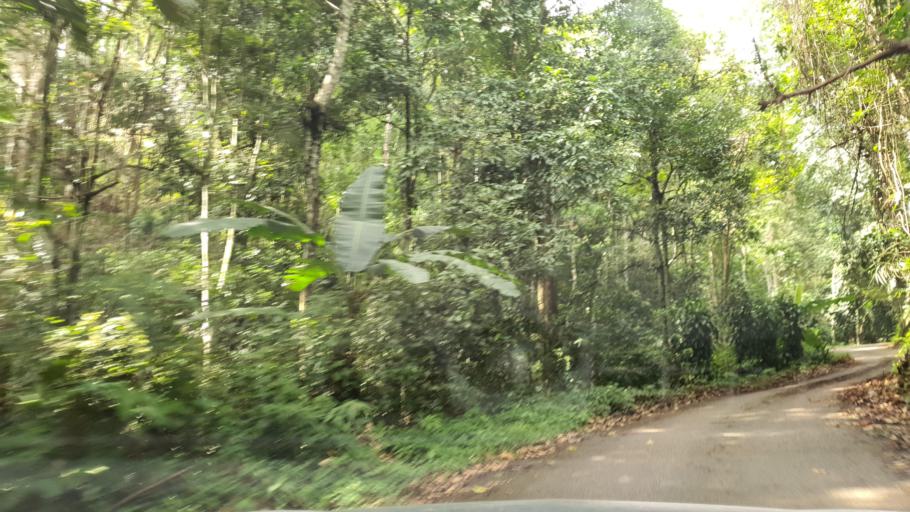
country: TH
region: Chiang Mai
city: Mae On
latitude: 18.9437
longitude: 99.3086
